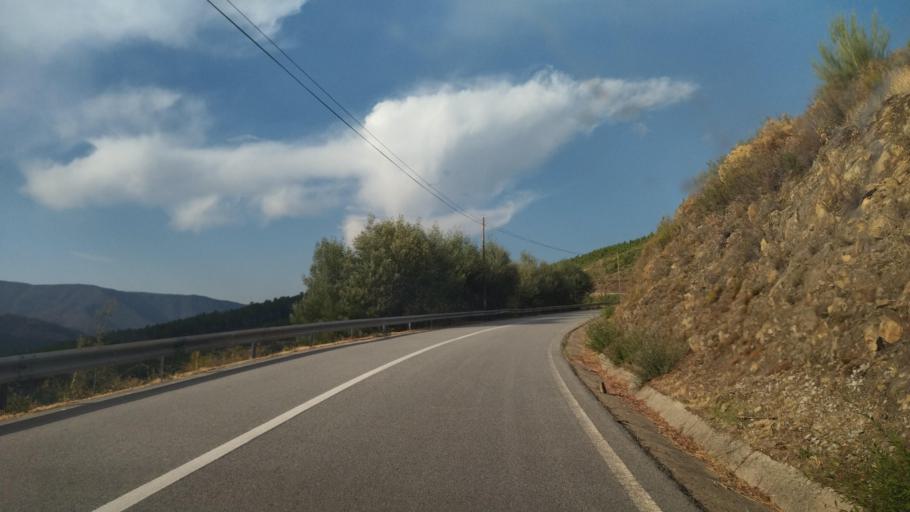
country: PT
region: Castelo Branco
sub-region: Covilha
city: Teixoso
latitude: 40.3693
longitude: -7.4485
